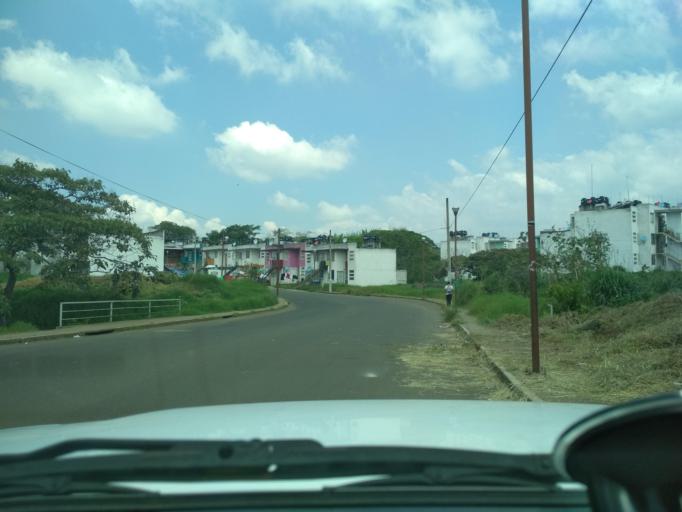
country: MX
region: Veracruz
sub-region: Fortin
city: Fraccionamiento los Alamos
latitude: 18.9300
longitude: -96.9754
